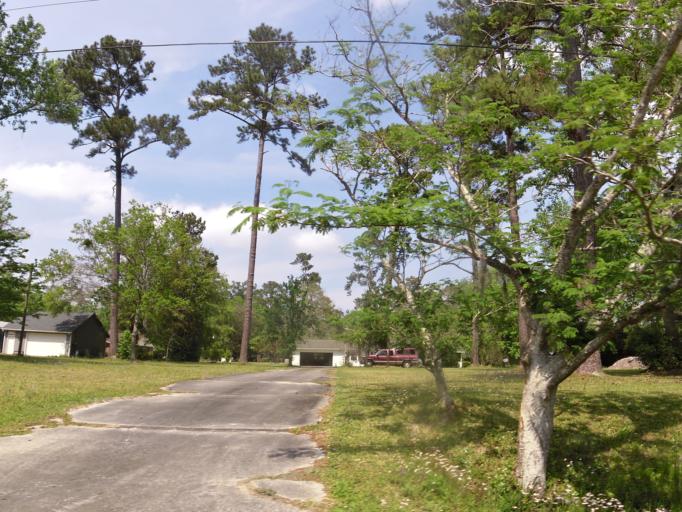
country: US
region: Georgia
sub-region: Camden County
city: Kingsland
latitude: 30.7835
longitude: -81.6977
